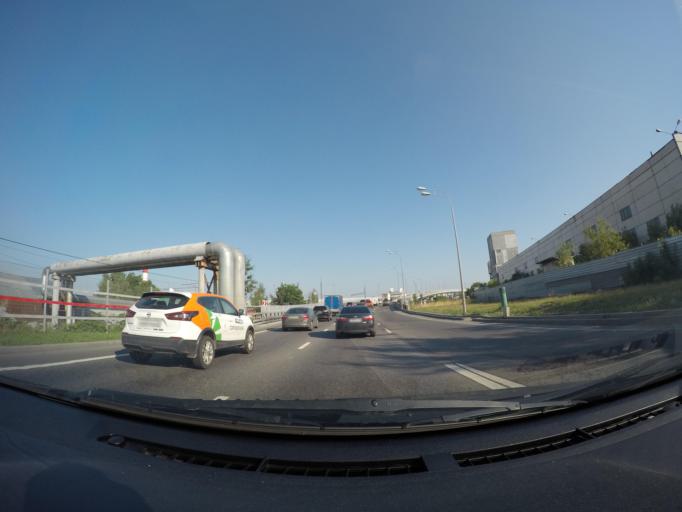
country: RU
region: Moscow
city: Ryazanskiy
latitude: 55.7490
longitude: 37.7483
